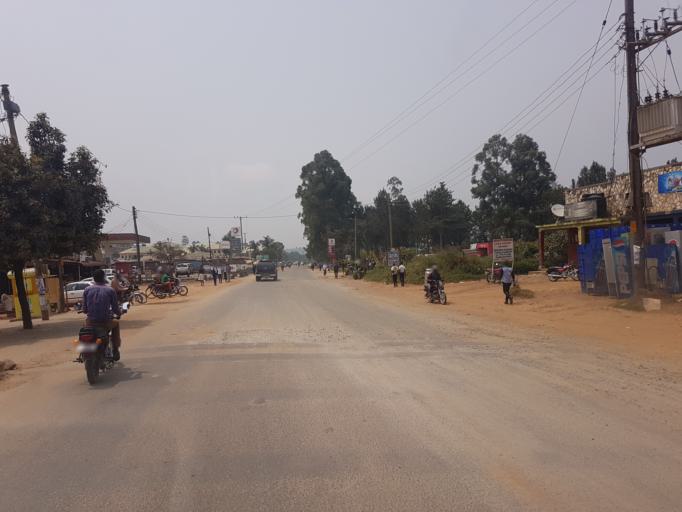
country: UG
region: Western Region
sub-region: Bushenyi District
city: Bushenyi
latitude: -0.5411
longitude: 30.1433
